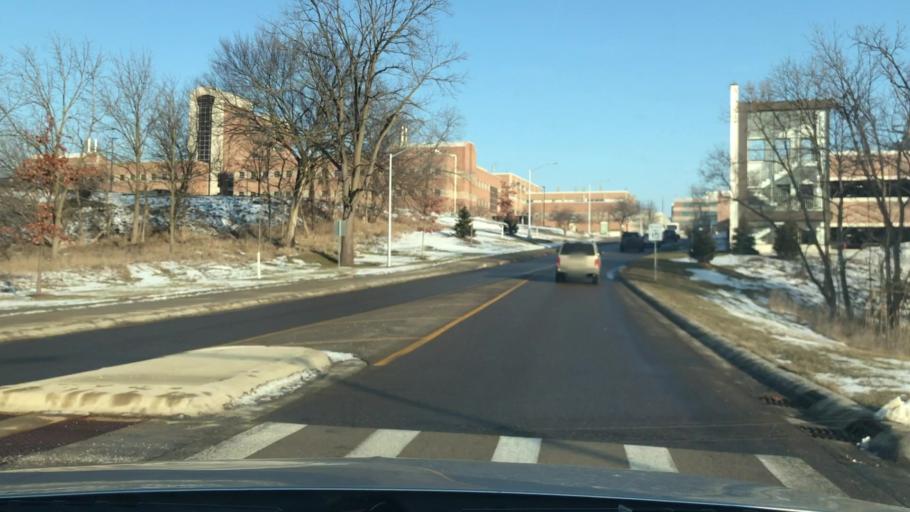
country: US
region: Michigan
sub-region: Oakland County
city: Auburn Hills
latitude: 42.6691
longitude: -83.2157
